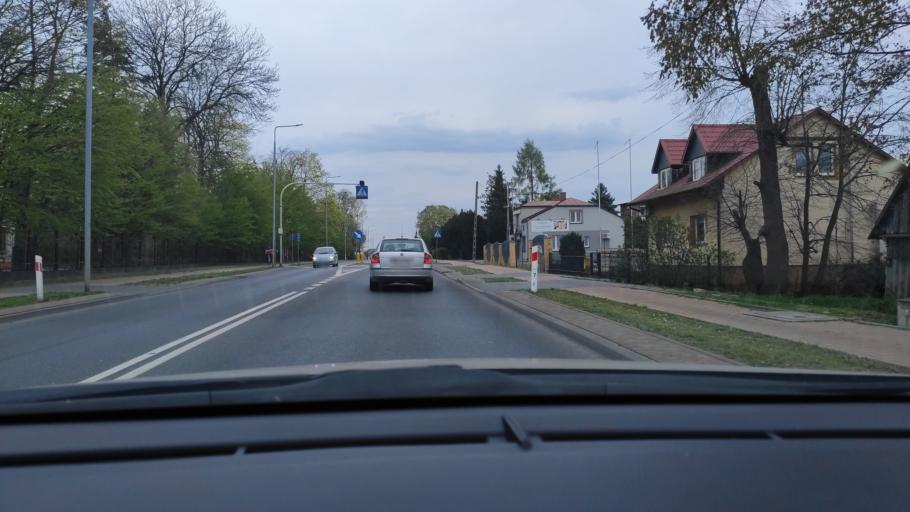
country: PL
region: Masovian Voivodeship
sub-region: Powiat zwolenski
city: Zwolen
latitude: 51.3583
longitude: 21.5697
